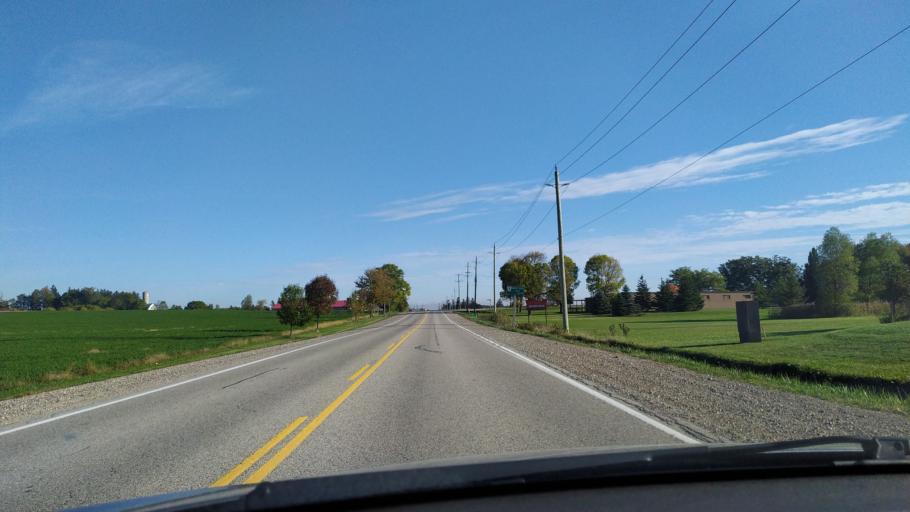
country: CA
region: Ontario
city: Stratford
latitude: 43.4772
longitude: -80.7810
